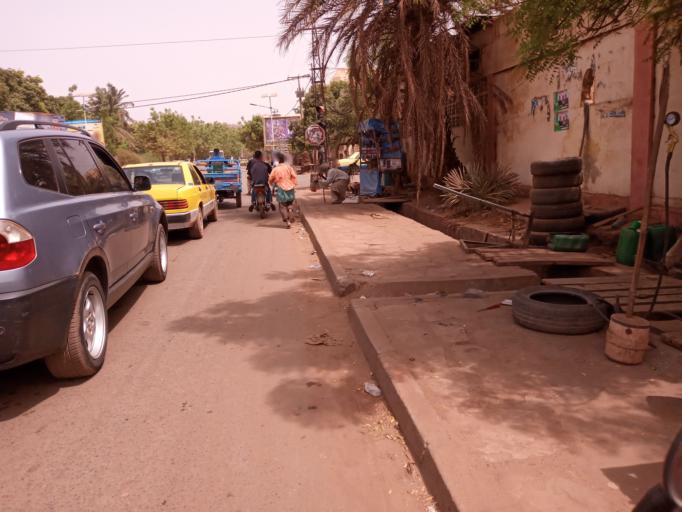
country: ML
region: Bamako
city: Bamako
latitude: 12.6475
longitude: -7.9803
